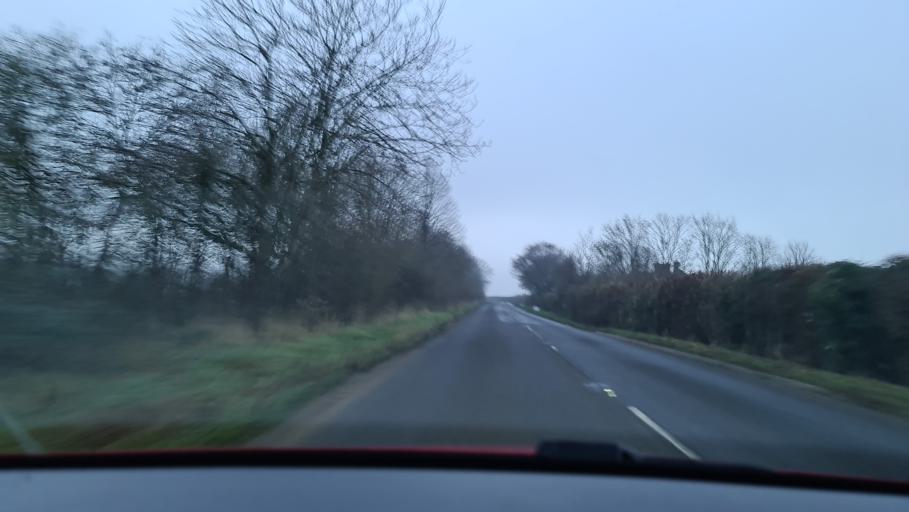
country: GB
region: England
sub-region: Oxfordshire
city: Bicester
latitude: 51.8947
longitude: -1.2108
